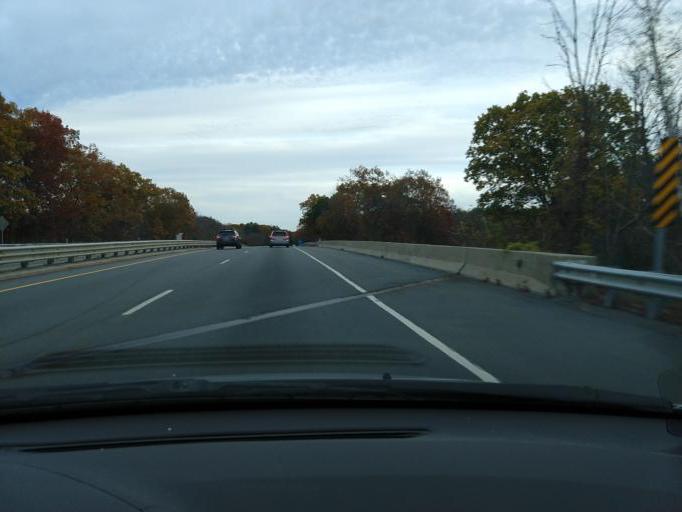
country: US
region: Massachusetts
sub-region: Middlesex County
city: Littleton Common
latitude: 42.5179
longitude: -71.5021
